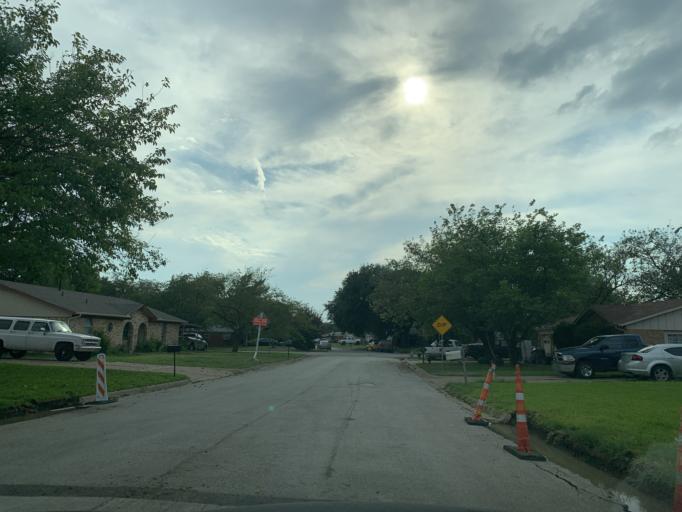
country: US
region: Texas
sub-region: Tarrant County
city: Watauga
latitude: 32.8634
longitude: -97.2382
